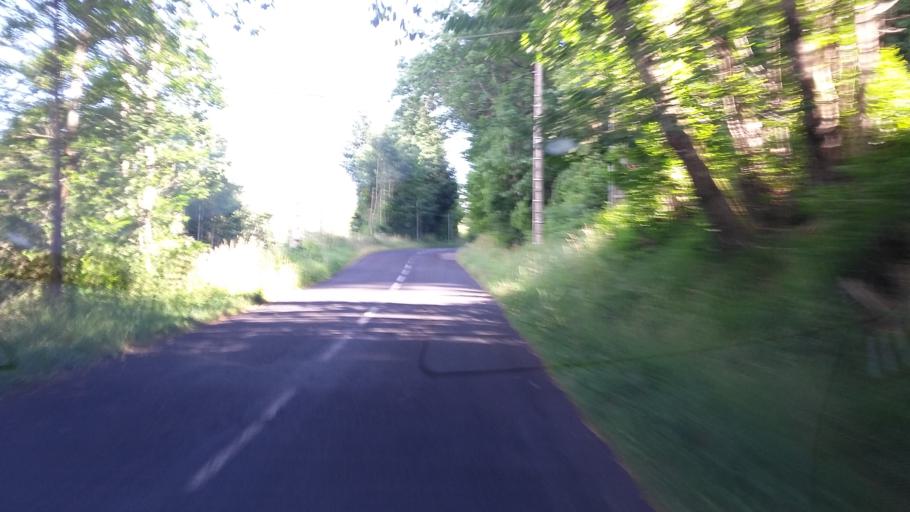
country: FR
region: Languedoc-Roussillon
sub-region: Departement de la Lozere
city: Meyrueis
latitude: 44.0150
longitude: 3.3635
